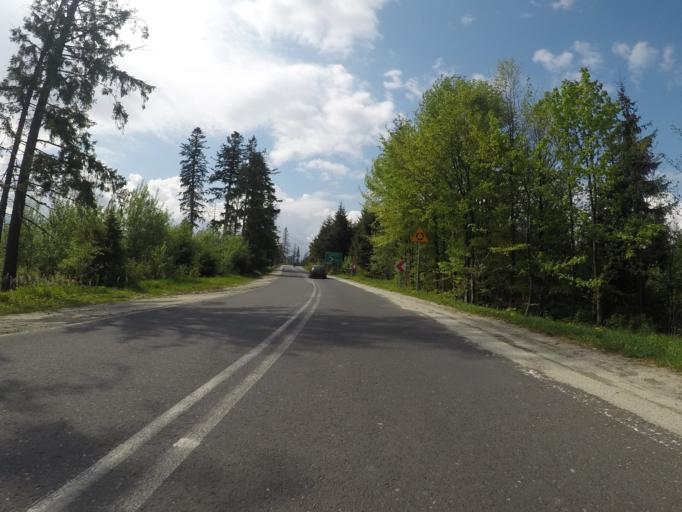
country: PL
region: Lesser Poland Voivodeship
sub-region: Powiat tatrzanski
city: Bukowina Tatrzanska
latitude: 49.2895
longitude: 20.1129
